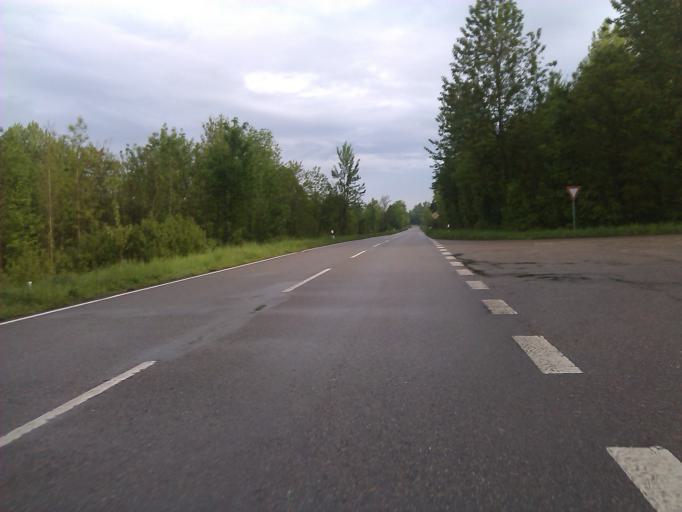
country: FR
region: Alsace
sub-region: Departement du Bas-Rhin
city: Drusenheim
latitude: 48.7489
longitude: 7.9734
